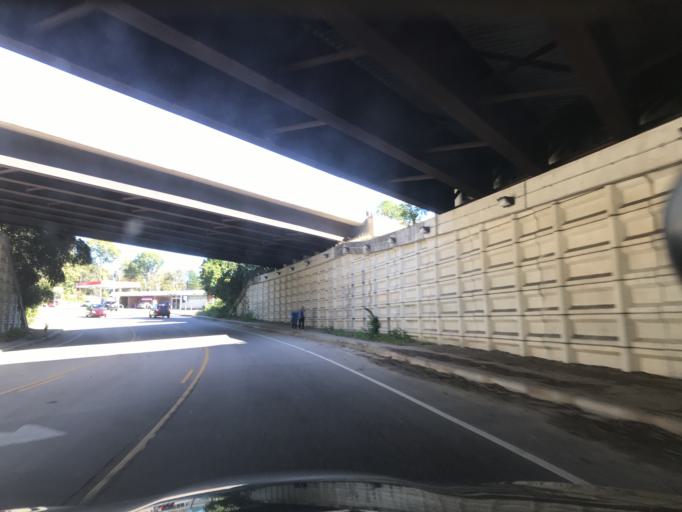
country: US
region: North Carolina
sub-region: Durham County
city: Durham
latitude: 36.0053
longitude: -78.9239
